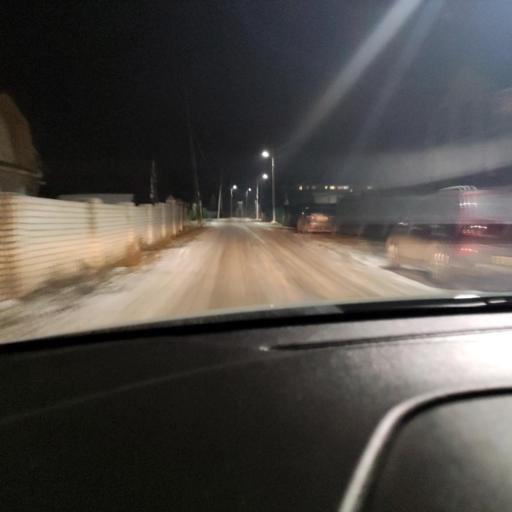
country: RU
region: Tatarstan
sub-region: Gorod Kazan'
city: Kazan
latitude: 55.7200
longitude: 49.0978
